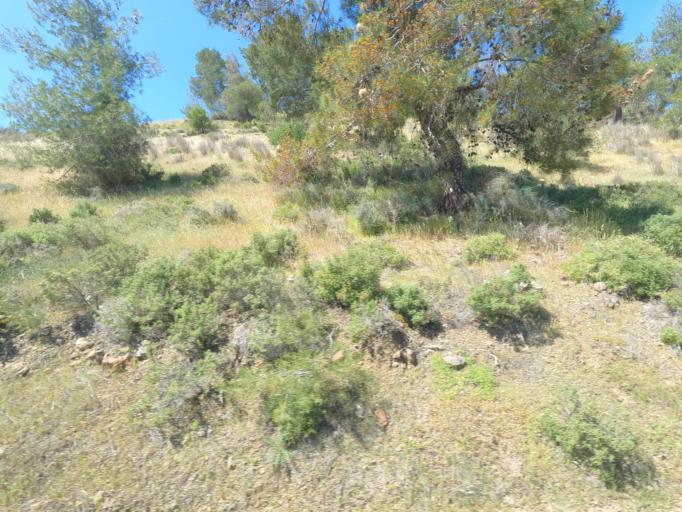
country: CY
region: Lefkosia
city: Peristerona
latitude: 35.0422
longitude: 33.0779
